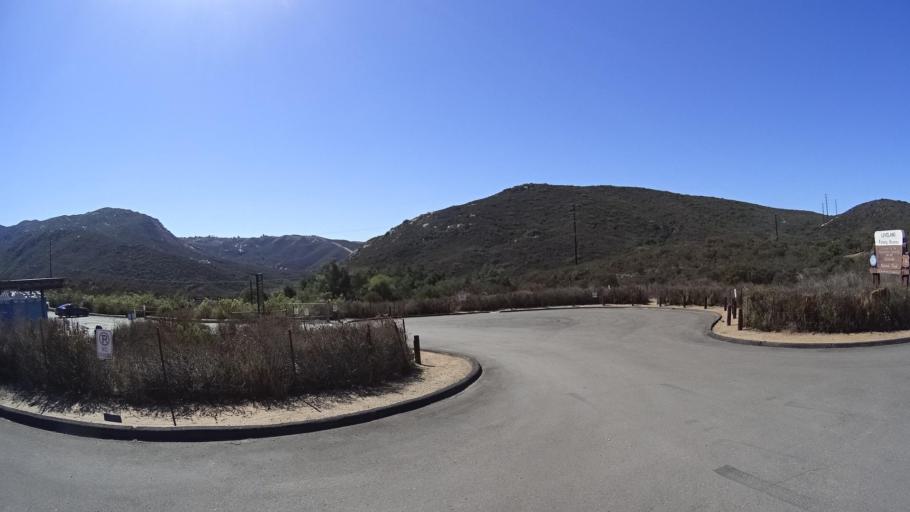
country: US
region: California
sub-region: San Diego County
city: Alpine
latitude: 32.8000
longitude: -116.7602
